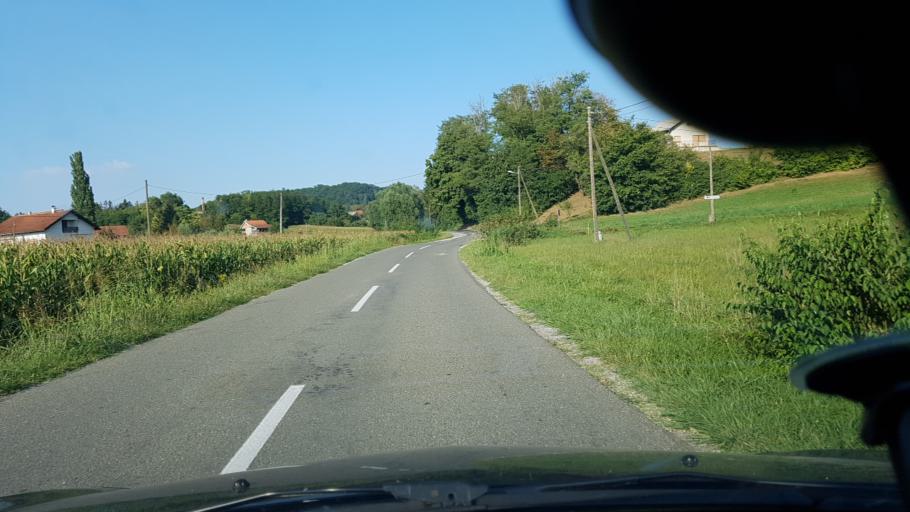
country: SI
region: Bistrica ob Sotli
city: Bistrica ob Sotli
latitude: 46.0212
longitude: 15.7269
